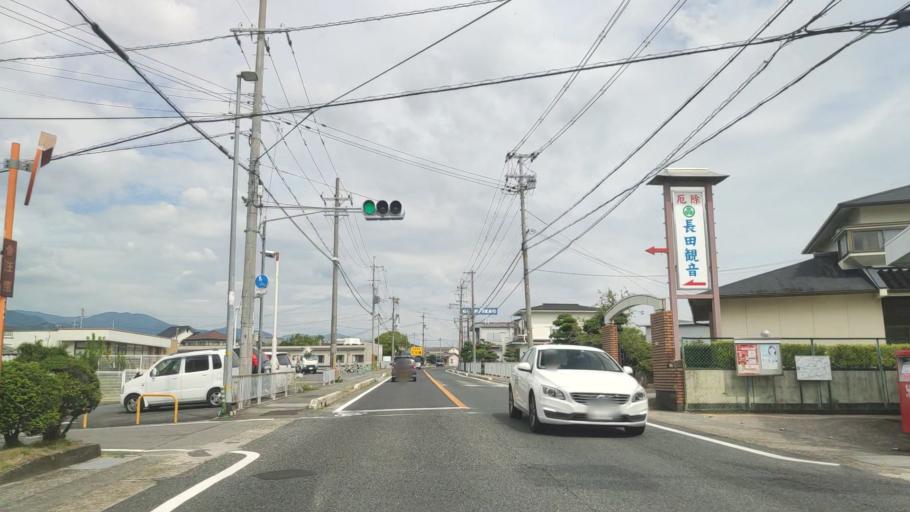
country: JP
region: Wakayama
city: Iwade
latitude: 34.2663
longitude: 135.3910
